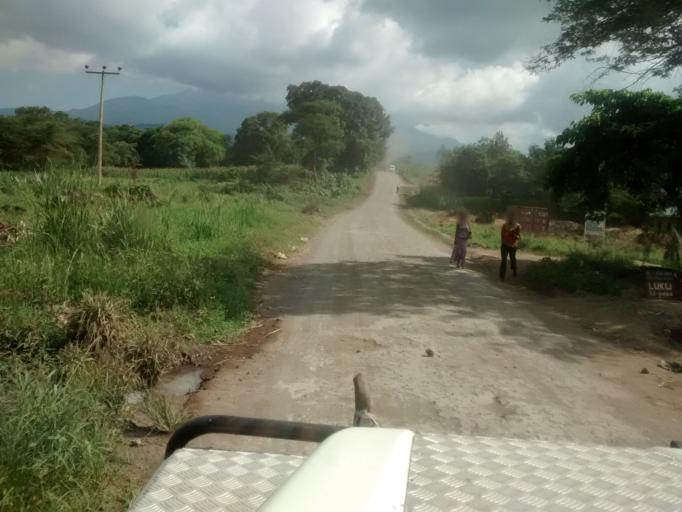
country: TZ
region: Arusha
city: Usa River
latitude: -3.3679
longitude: 36.8464
